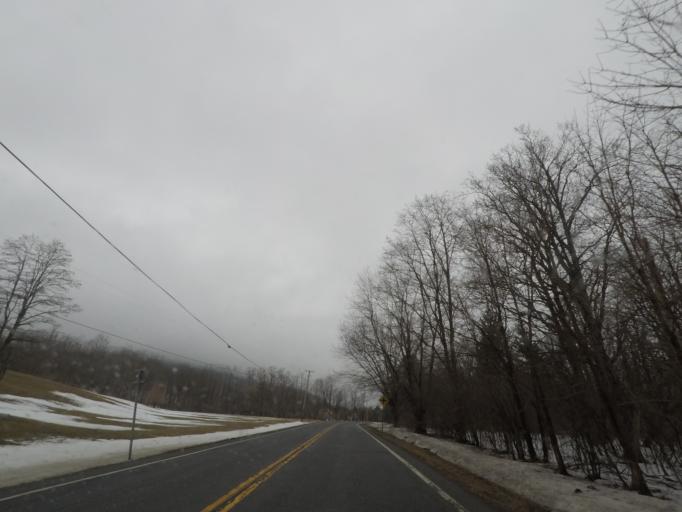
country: US
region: New York
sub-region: Albany County
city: Altamont
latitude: 42.6652
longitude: -74.0023
